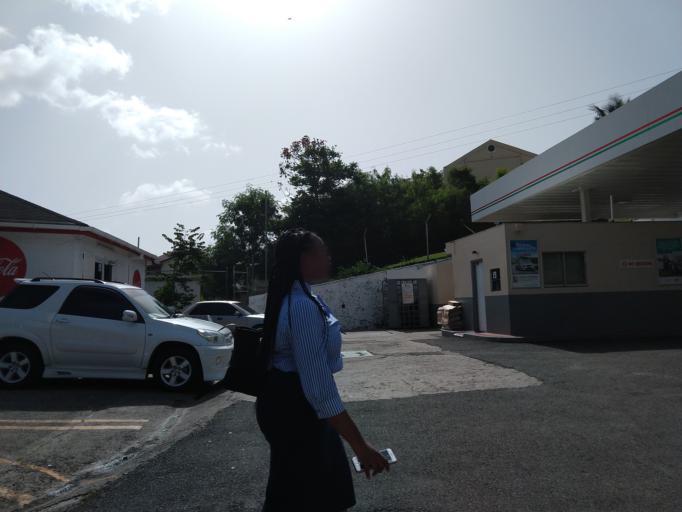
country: GD
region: Saint George
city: Saint George's
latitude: 12.0467
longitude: -61.7452
